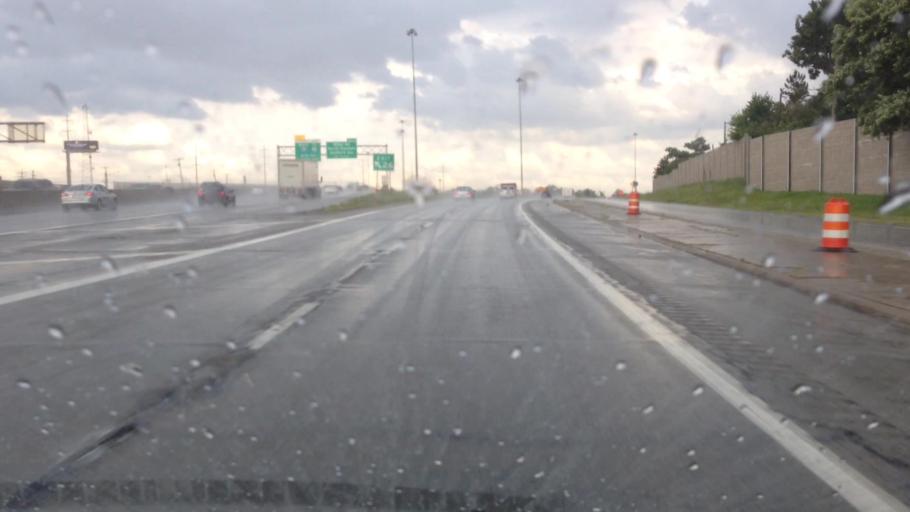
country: US
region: Ohio
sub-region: Cuyahoga County
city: Bedford Heights
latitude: 41.4242
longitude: -81.5322
